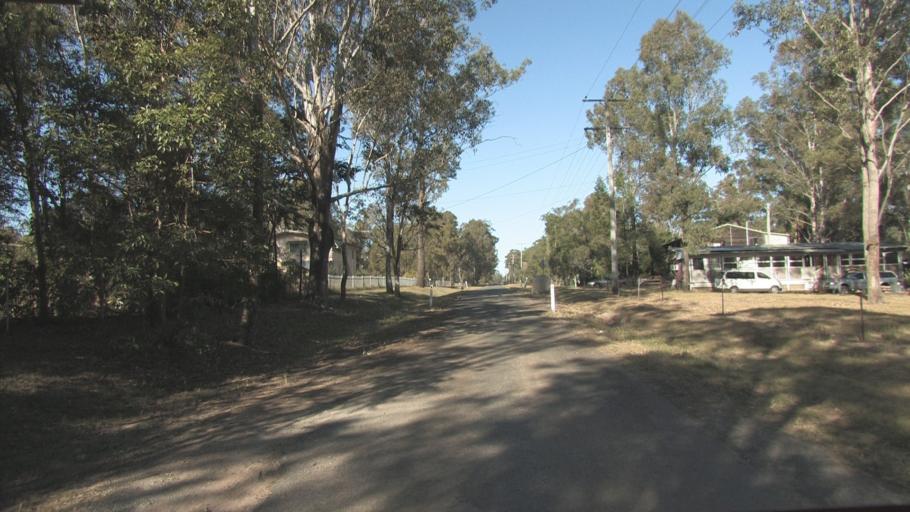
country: AU
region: Queensland
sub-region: Logan
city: Park Ridge South
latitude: -27.7498
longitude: 153.0347
